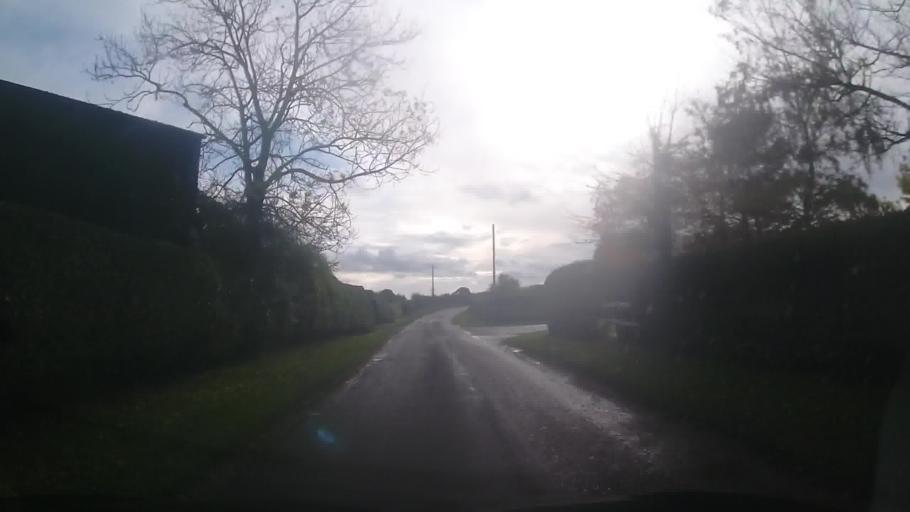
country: GB
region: England
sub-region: Shropshire
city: Whitchurch
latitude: 52.9484
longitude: -2.6997
